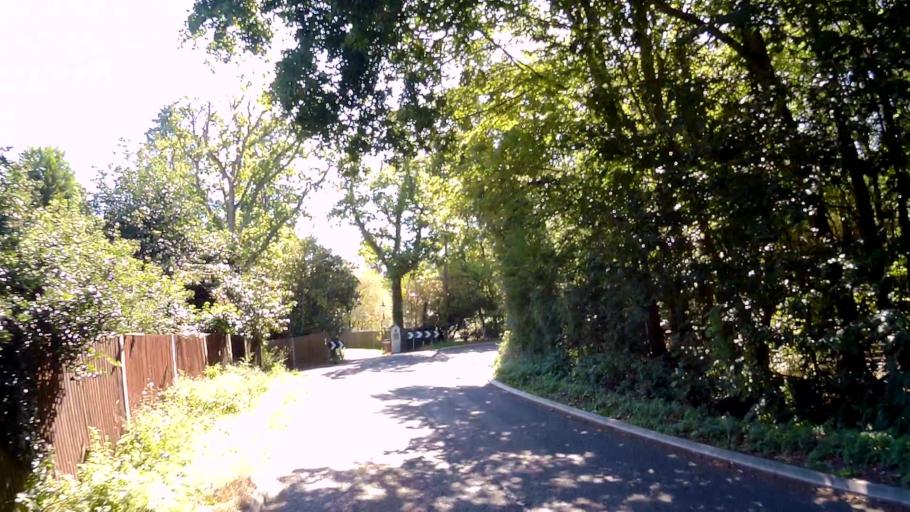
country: GB
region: England
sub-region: Wokingham
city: Barkham
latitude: 51.3828
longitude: -0.8850
